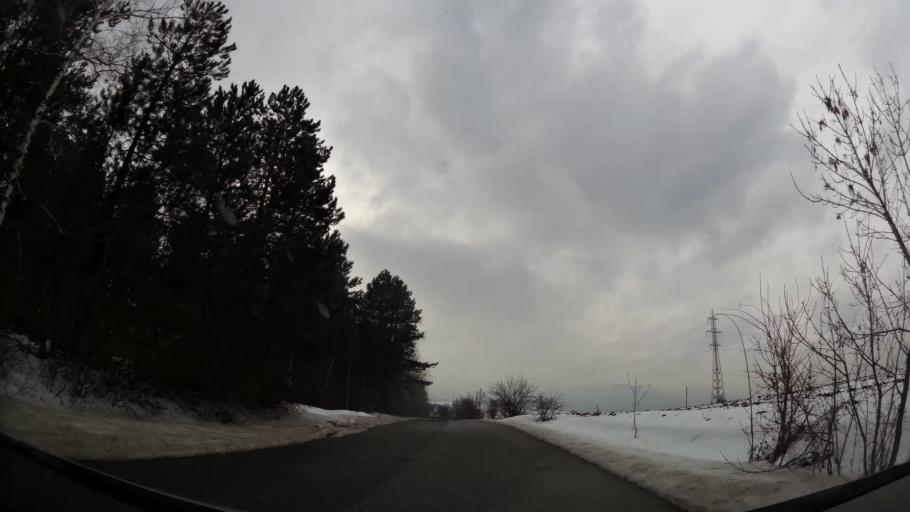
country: BG
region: Sofiya
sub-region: Obshtina Bozhurishte
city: Bozhurishte
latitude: 42.6650
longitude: 23.2149
